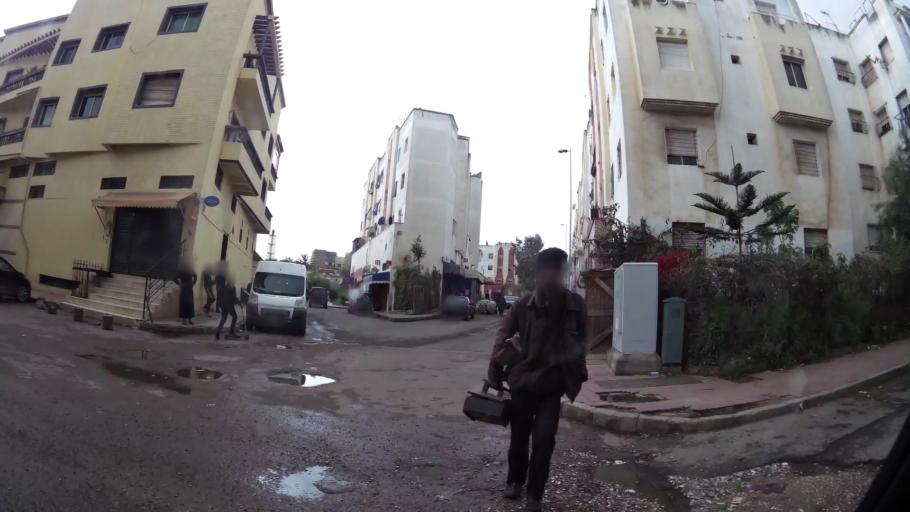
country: MA
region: Grand Casablanca
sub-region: Casablanca
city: Casablanca
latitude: 33.5438
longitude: -7.6825
